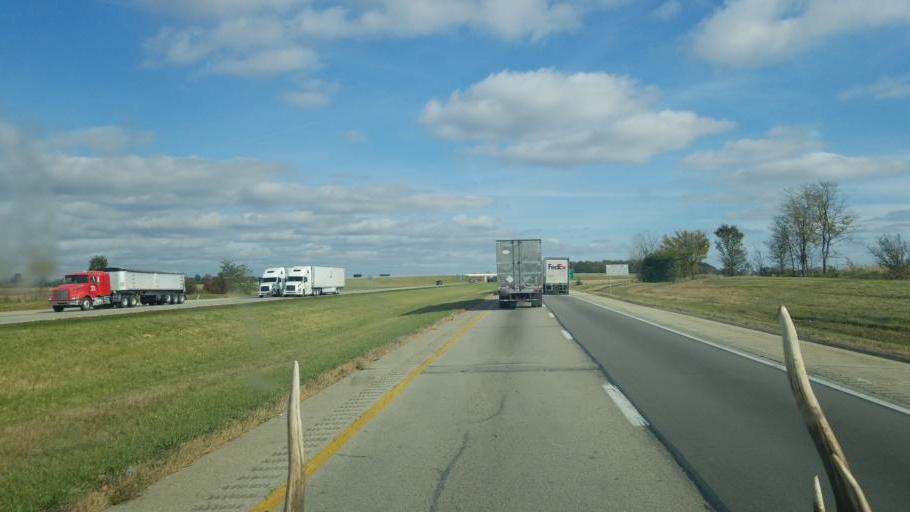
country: US
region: Ohio
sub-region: Preble County
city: New Paris
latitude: 39.8285
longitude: -84.7892
